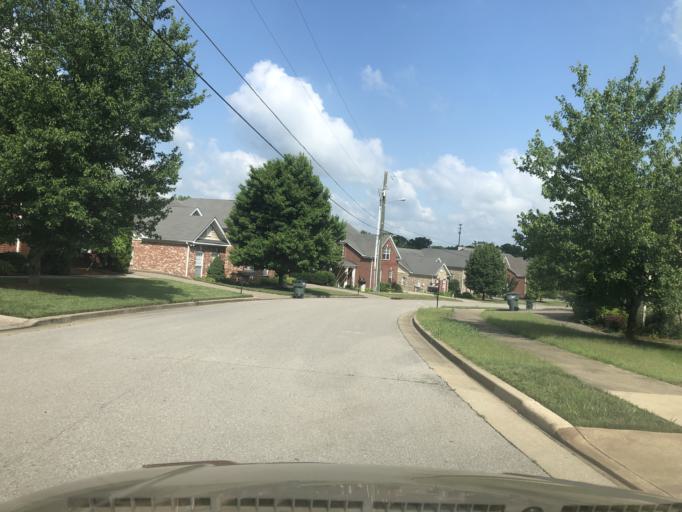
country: US
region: Tennessee
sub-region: Wilson County
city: Green Hill
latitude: 36.2278
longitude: -86.5937
